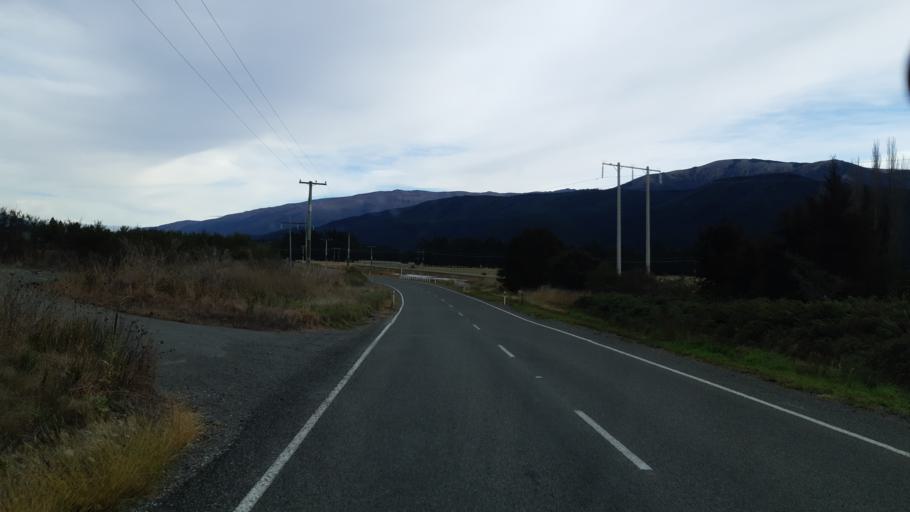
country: NZ
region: Tasman
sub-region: Tasman District
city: Brightwater
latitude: -41.6631
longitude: 173.2125
